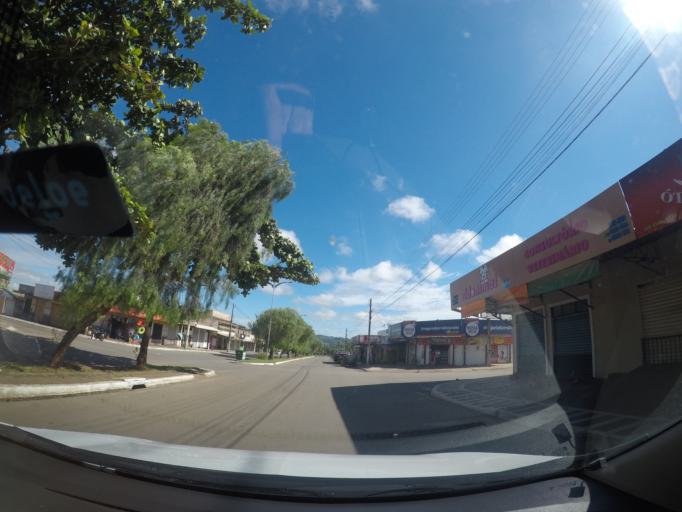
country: BR
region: Goias
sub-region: Senador Canedo
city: Senador Canedo
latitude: -16.6511
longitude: -49.1567
